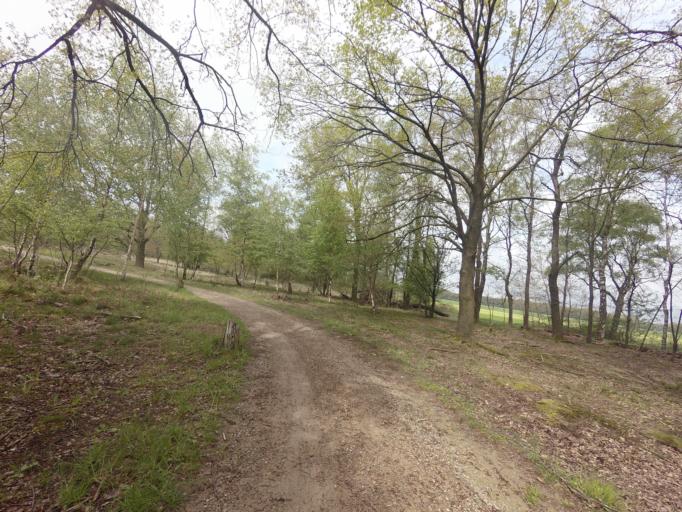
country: NL
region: Overijssel
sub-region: Gemeente Haaksbergen
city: Haaksbergen
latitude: 52.1358
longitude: 6.7882
